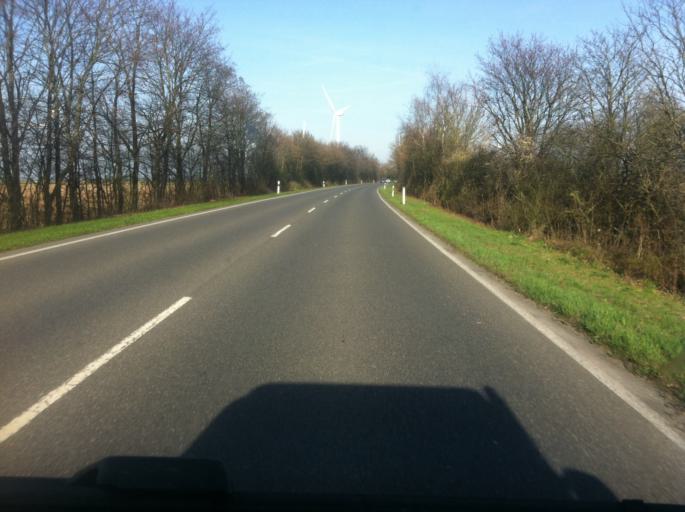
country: DE
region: North Rhine-Westphalia
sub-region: Regierungsbezirk Koln
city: Norvenich
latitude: 50.7635
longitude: 6.6631
